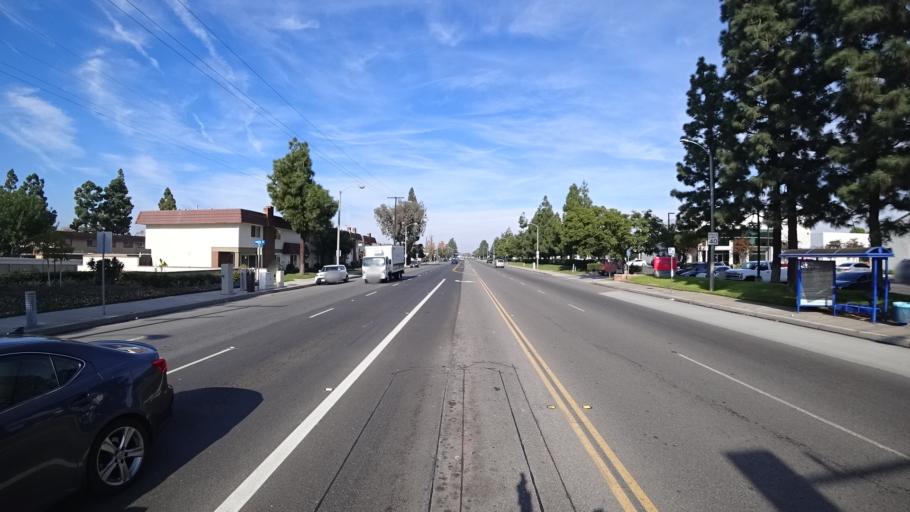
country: US
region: California
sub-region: Orange County
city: Stanton
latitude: 33.7960
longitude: -118.0111
